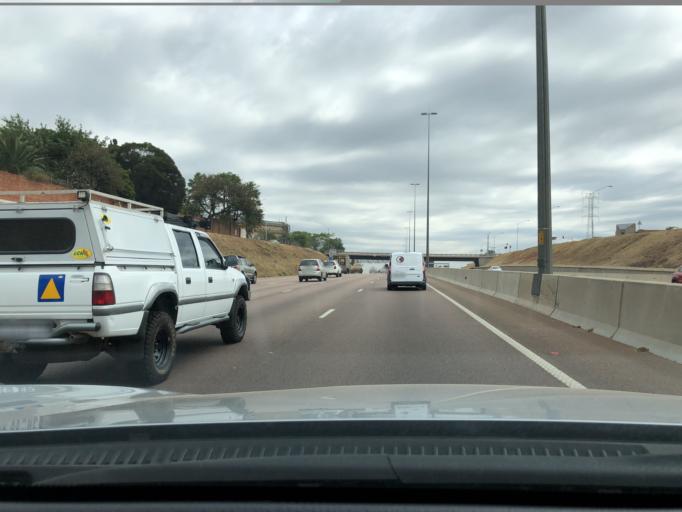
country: ZA
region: Gauteng
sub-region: City of Tshwane Metropolitan Municipality
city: Pretoria
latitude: -25.7591
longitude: 28.2750
